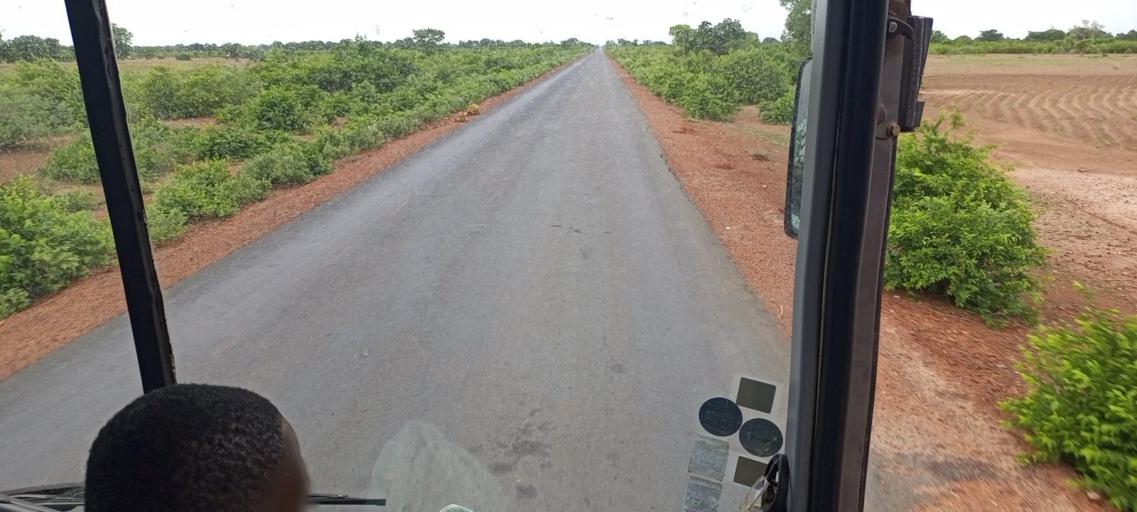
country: ML
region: Sikasso
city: Koutiala
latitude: 12.5665
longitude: -5.5983
